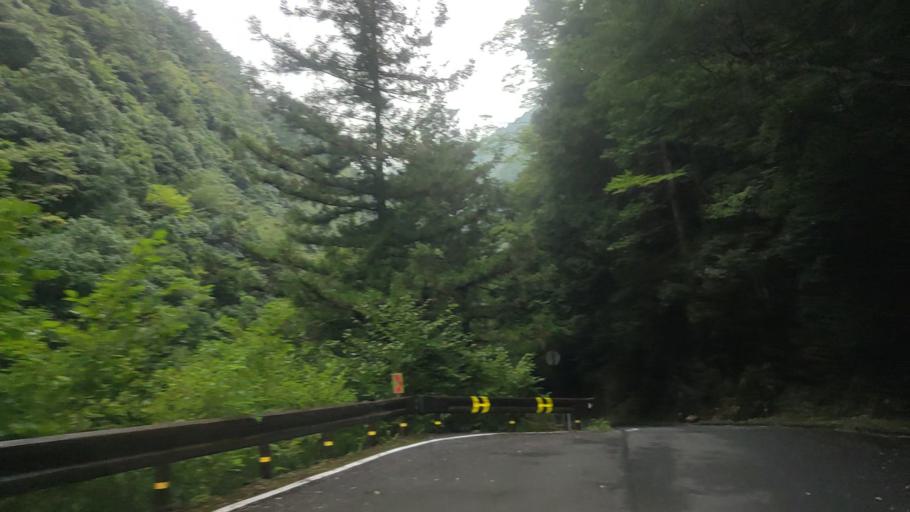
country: JP
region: Wakayama
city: Koya
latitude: 34.2435
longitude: 135.6519
